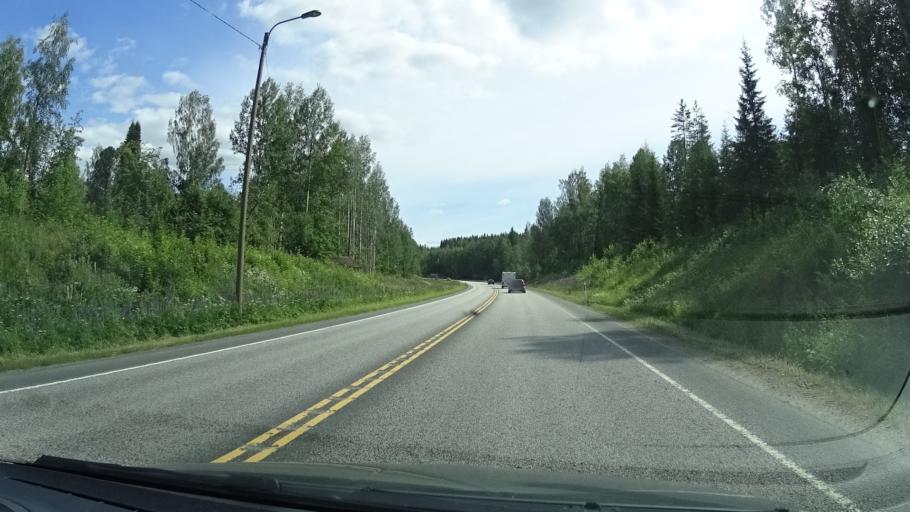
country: FI
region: Central Finland
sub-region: Jyvaeskylae
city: Jyvaeskylae
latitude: 62.2661
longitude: 25.5610
